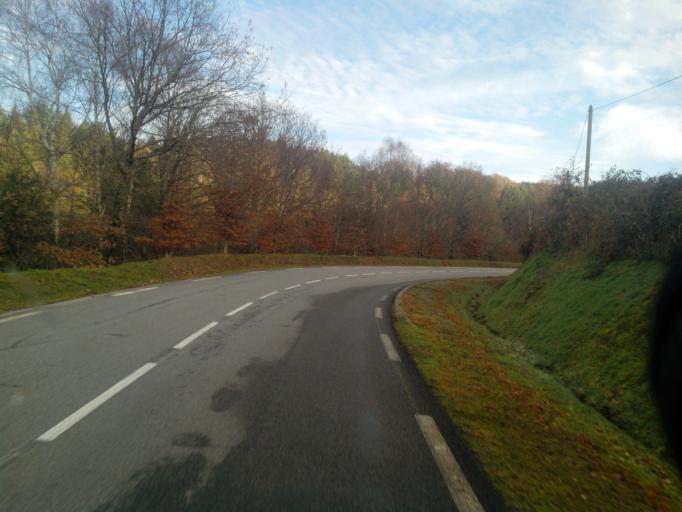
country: FR
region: Limousin
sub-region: Departement de la Haute-Vienne
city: Eymoutiers
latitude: 45.6866
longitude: 1.7913
